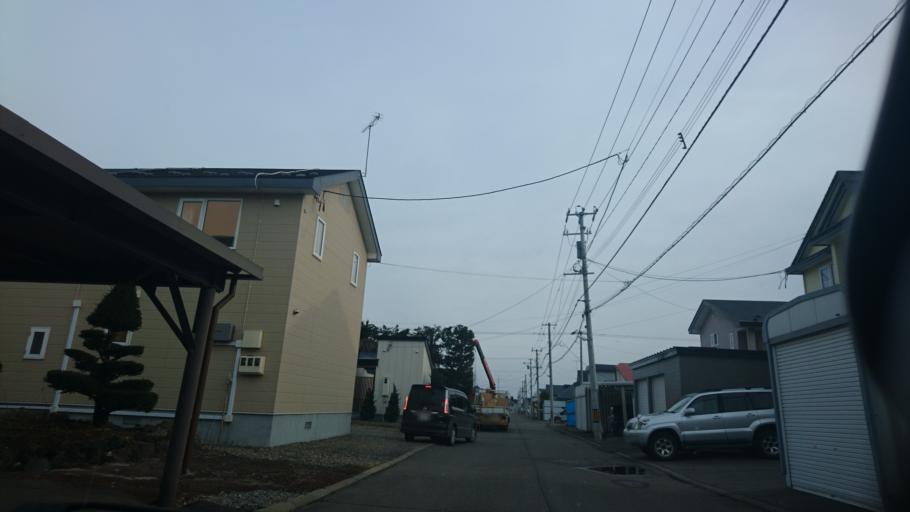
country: JP
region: Hokkaido
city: Otofuke
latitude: 43.0004
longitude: 143.1902
